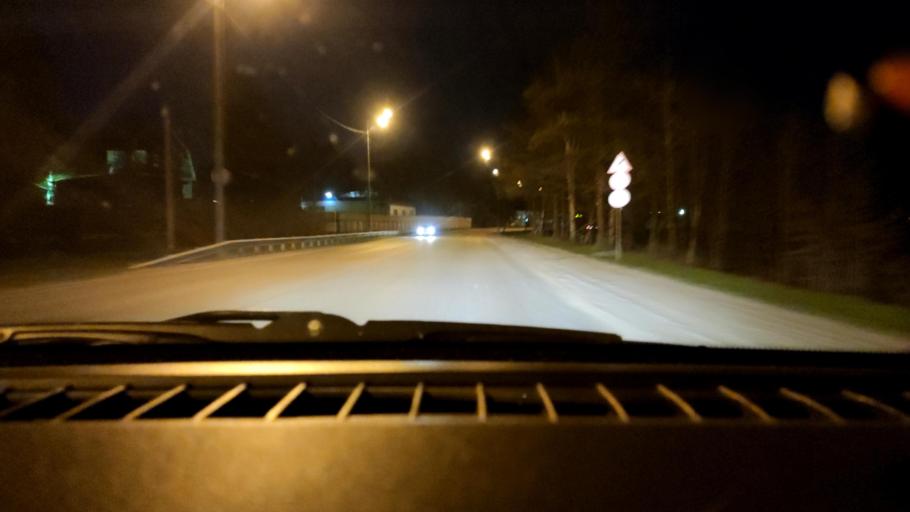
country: RU
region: Perm
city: Kondratovo
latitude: 58.0374
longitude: 56.1593
